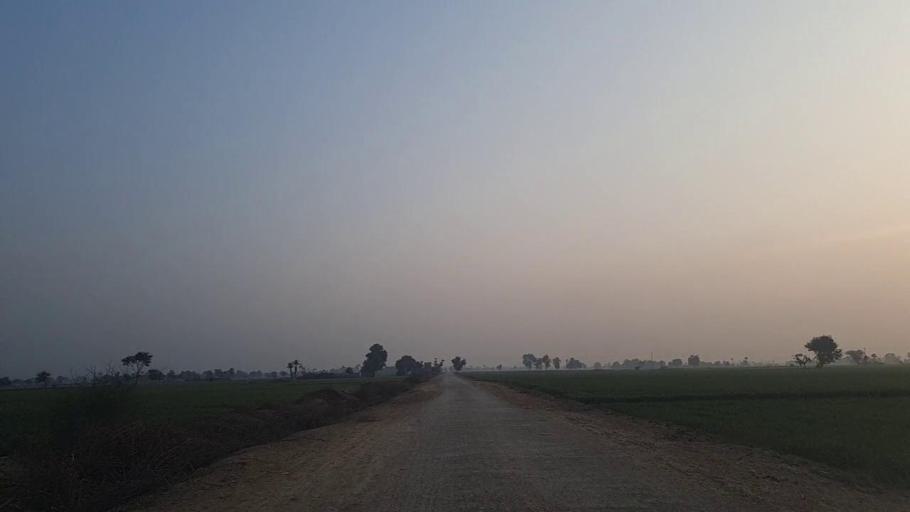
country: PK
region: Sindh
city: Nawabshah
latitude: 26.2692
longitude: 68.4569
